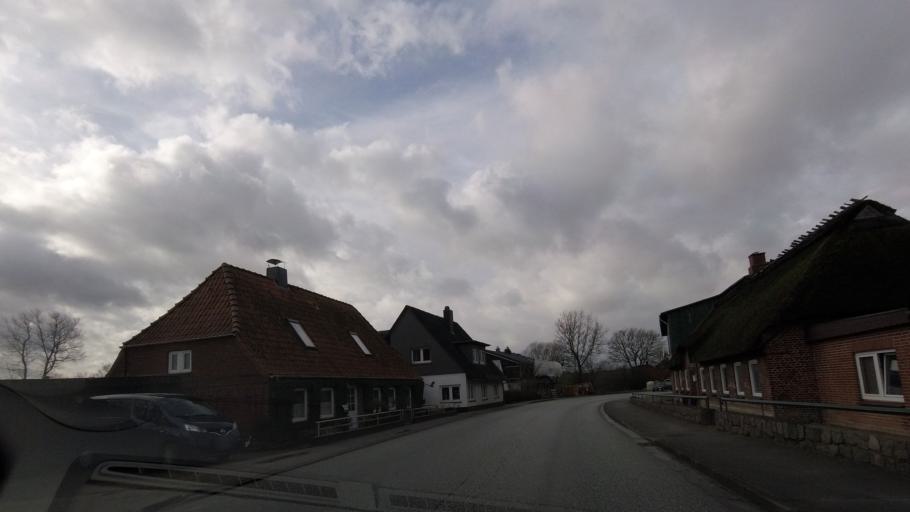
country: DE
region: Schleswig-Holstein
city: Dollrottfeld
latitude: 54.6425
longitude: 9.8154
